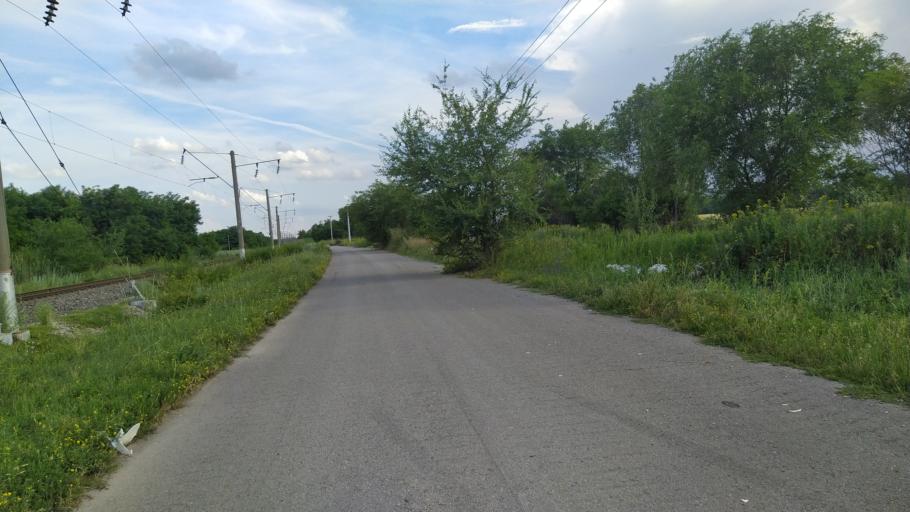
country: RU
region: Rostov
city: Bataysk
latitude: 47.1110
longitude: 39.7113
